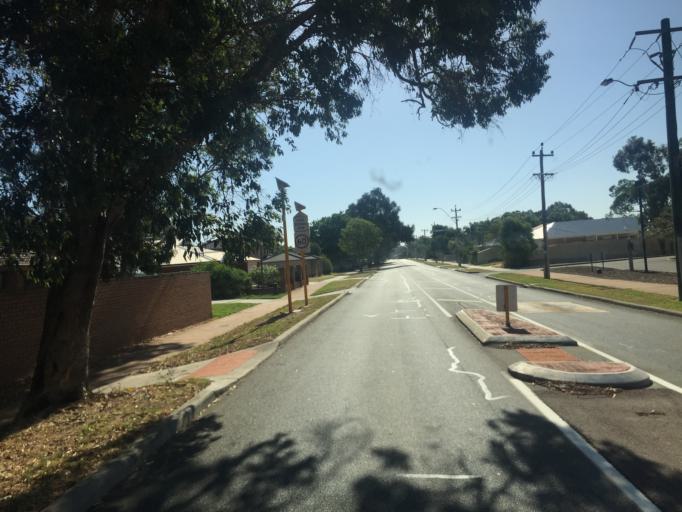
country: AU
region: Western Australia
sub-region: Gosnells
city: Kenwick
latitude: -32.0343
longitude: 115.9787
